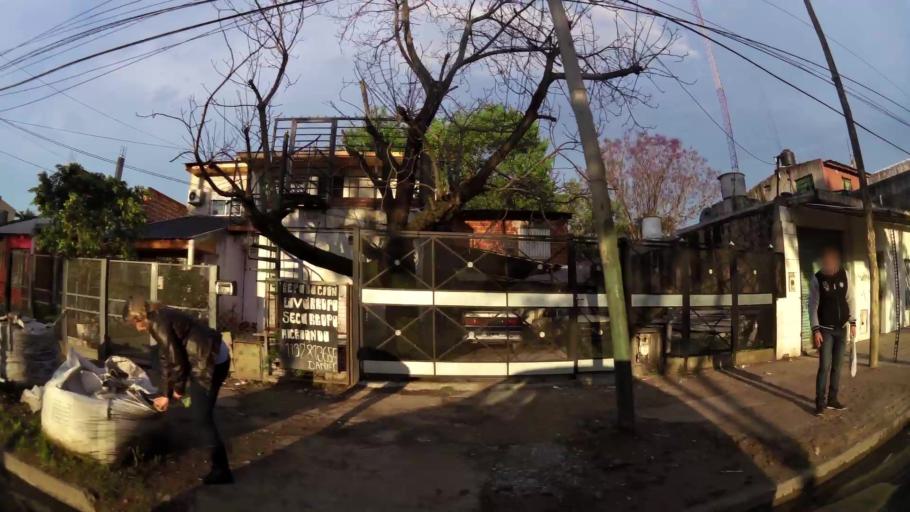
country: AR
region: Buenos Aires
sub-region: Partido de Almirante Brown
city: Adrogue
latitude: -34.7682
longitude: -58.3398
